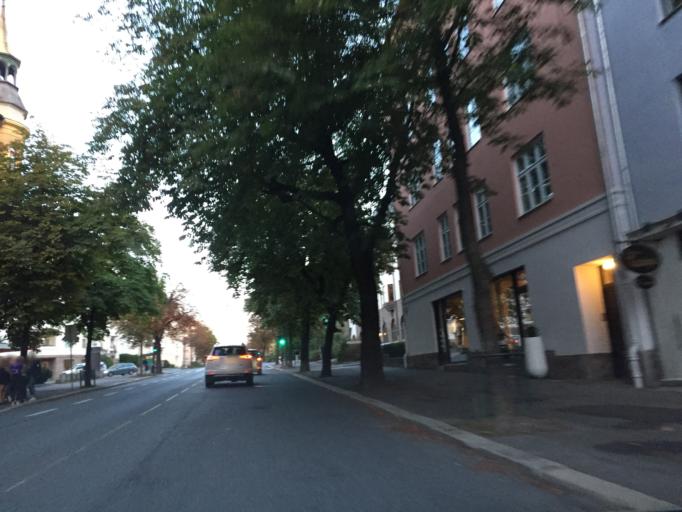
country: NO
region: Oslo
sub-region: Oslo
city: Sjolyststranda
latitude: 59.9183
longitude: 10.7052
